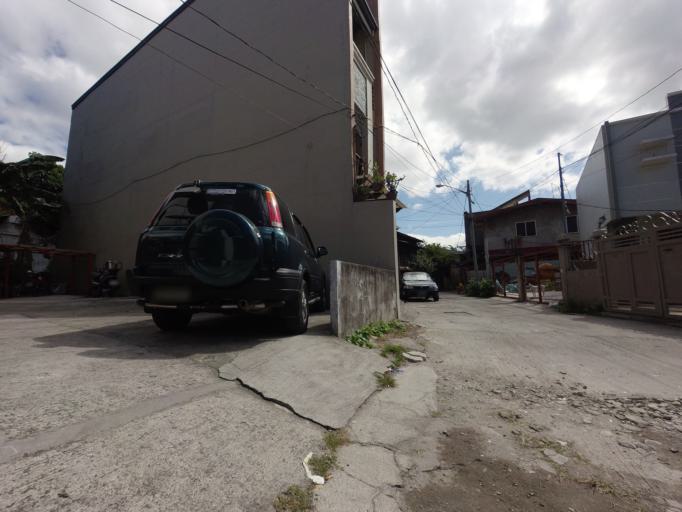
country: PH
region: Metro Manila
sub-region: San Juan
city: San Juan
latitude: 14.5872
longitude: 121.0221
